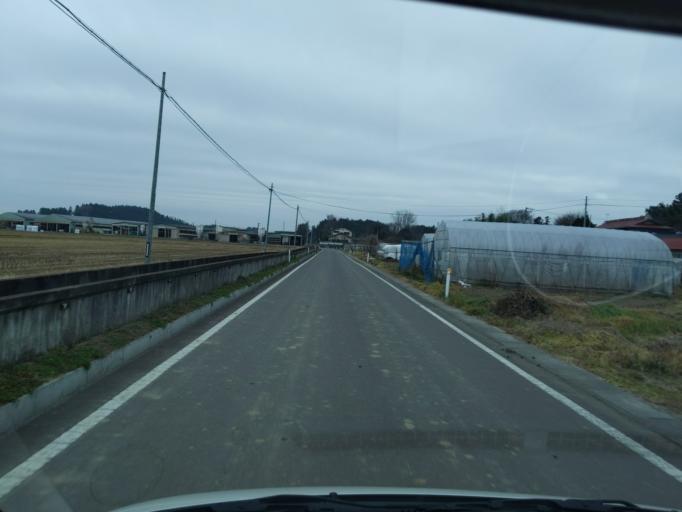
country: JP
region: Iwate
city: Ichinoseki
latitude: 38.7378
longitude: 141.2251
